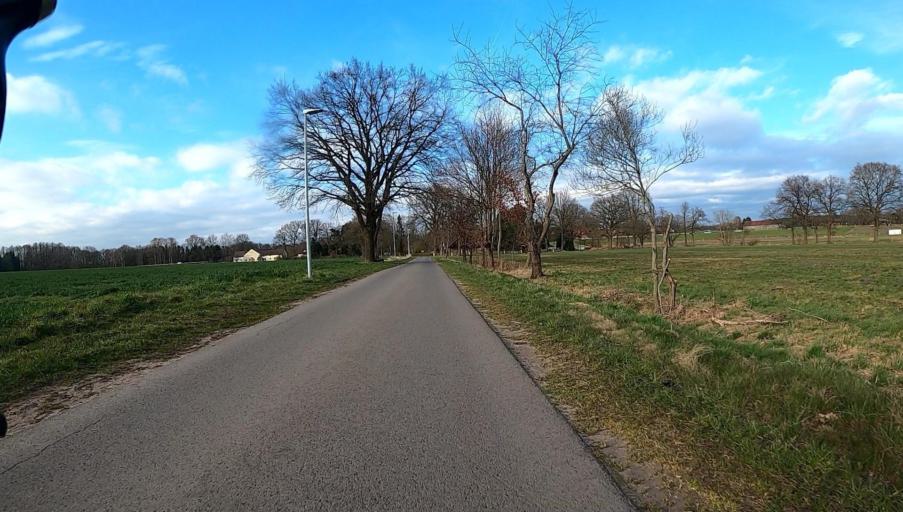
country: DE
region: Lower Saxony
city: Lindwedel
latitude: 52.5461
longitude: 9.6330
